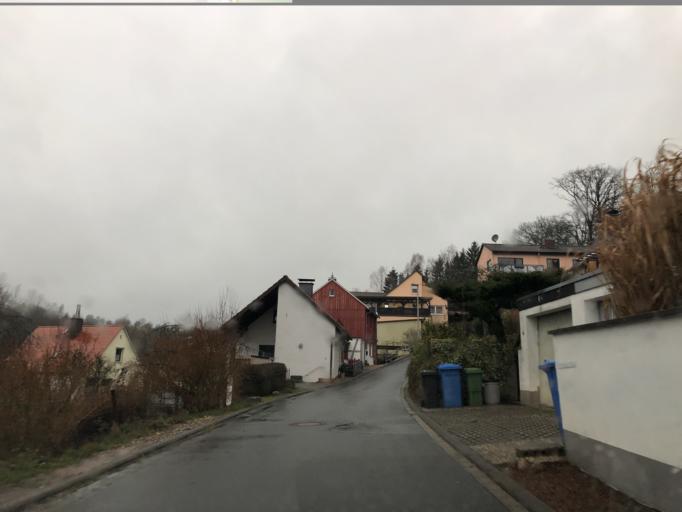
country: DE
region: Bavaria
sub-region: Regierungsbezirk Unterfranken
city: Rudenau
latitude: 49.7100
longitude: 9.1046
